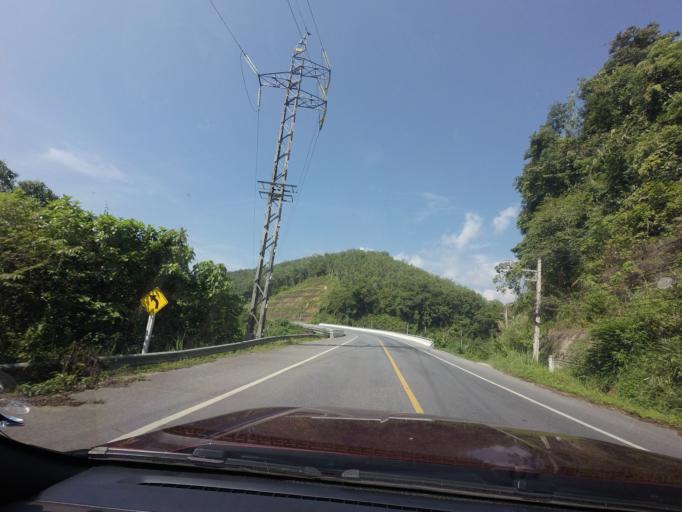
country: TH
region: Yala
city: Than To
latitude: 5.9579
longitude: 101.1928
